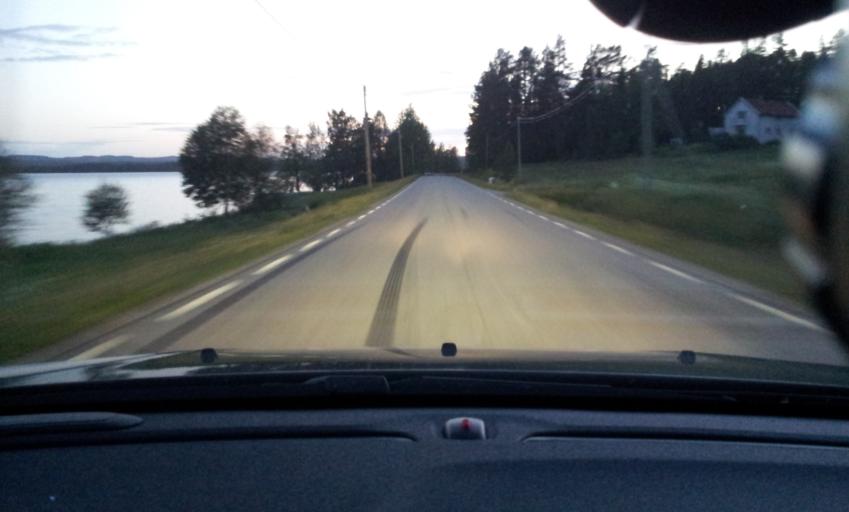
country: SE
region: Jaemtland
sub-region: Braecke Kommun
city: Braecke
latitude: 62.7415
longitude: 15.1049
